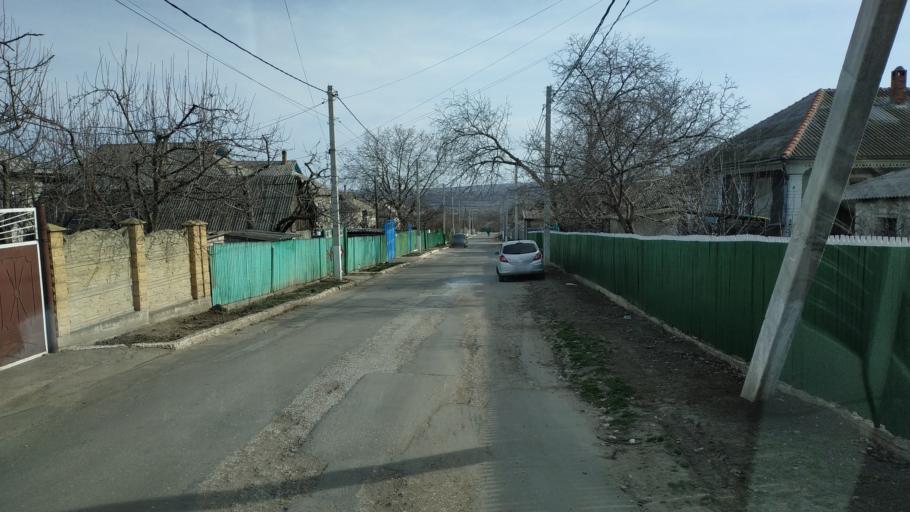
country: MD
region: Chisinau
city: Vatra
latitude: 47.0780
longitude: 28.6863
